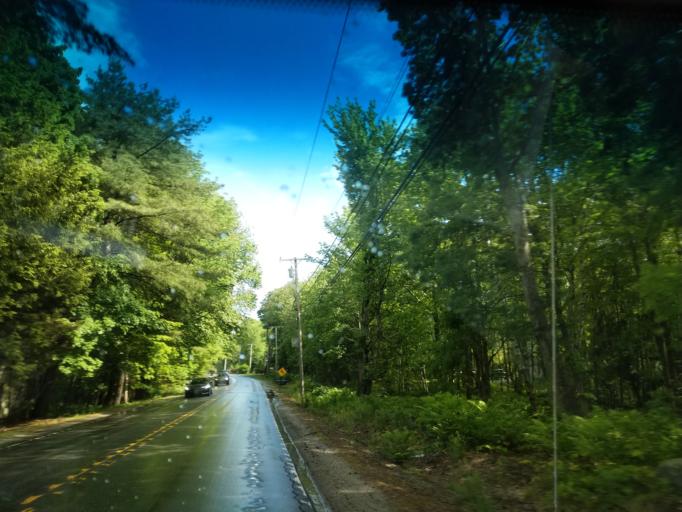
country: US
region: Maine
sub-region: Cumberland County
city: Cumberland Center
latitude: 43.7712
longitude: -70.3314
